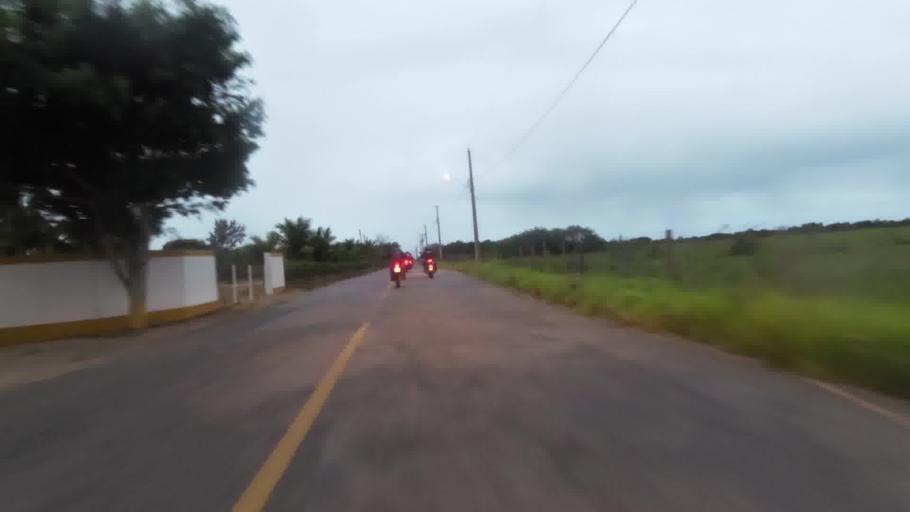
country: BR
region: Espirito Santo
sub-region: Itapemirim
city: Itapemirim
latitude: -20.9795
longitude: -40.8169
